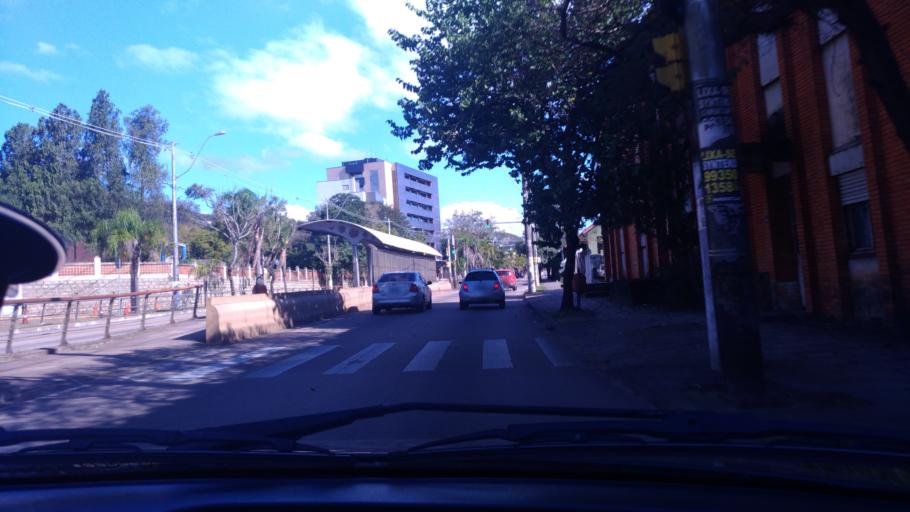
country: BR
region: Rio Grande do Sul
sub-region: Porto Alegre
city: Porto Alegre
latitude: -30.0701
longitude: -51.1891
